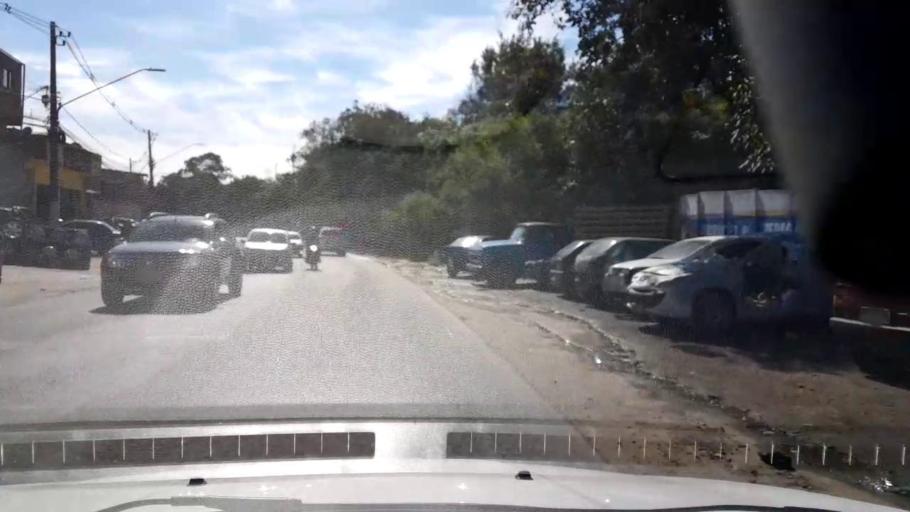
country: BR
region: Sao Paulo
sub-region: Ferraz De Vasconcelos
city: Ferraz de Vasconcelos
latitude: -23.5800
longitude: -46.4153
